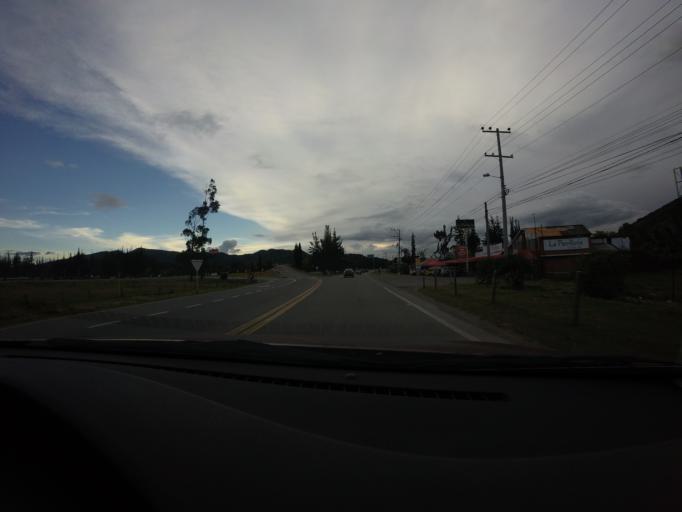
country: CO
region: Cundinamarca
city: Sopo
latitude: 4.9406
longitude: -73.9642
